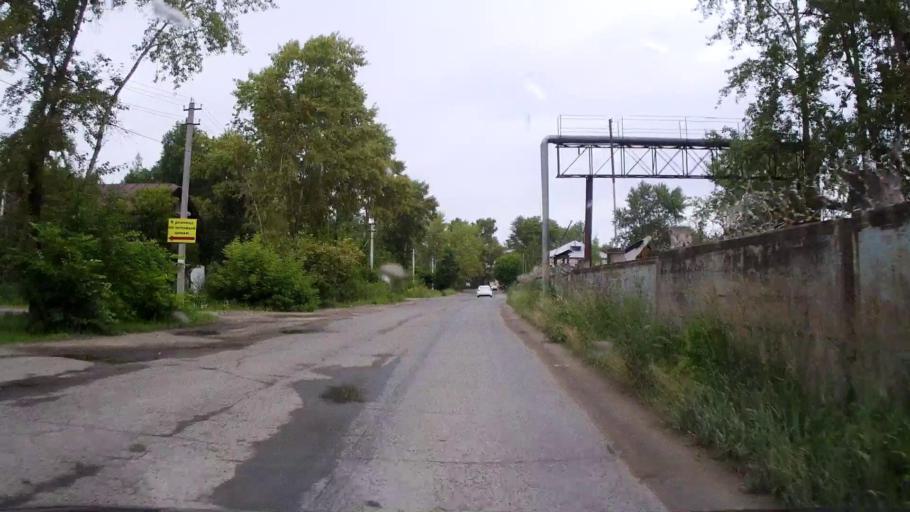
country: RU
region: Vologda
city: Vologda
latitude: 59.2035
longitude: 39.8771
